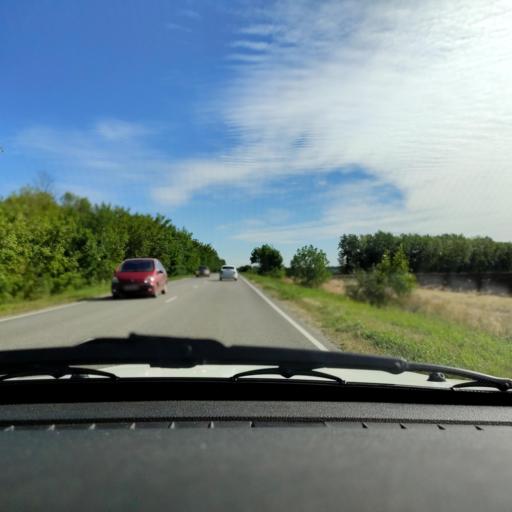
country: RU
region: Voronezj
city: Volya
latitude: 51.7108
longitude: 39.5295
